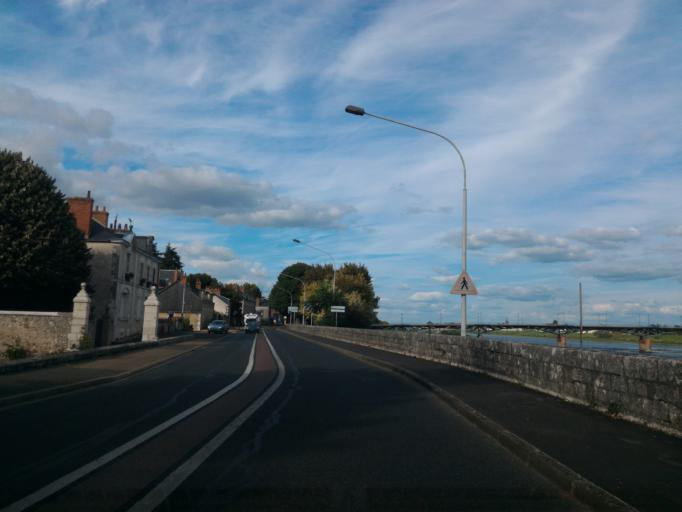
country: FR
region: Centre
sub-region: Departement du Loir-et-Cher
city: Blois
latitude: 47.5757
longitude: 1.3174
